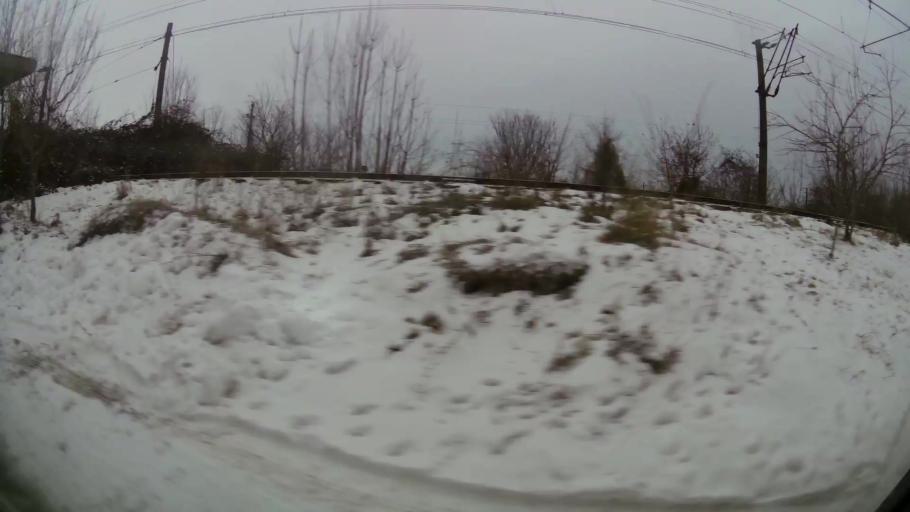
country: RO
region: Prahova
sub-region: Comuna Berceni
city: Corlatesti
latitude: 44.9247
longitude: 26.0660
